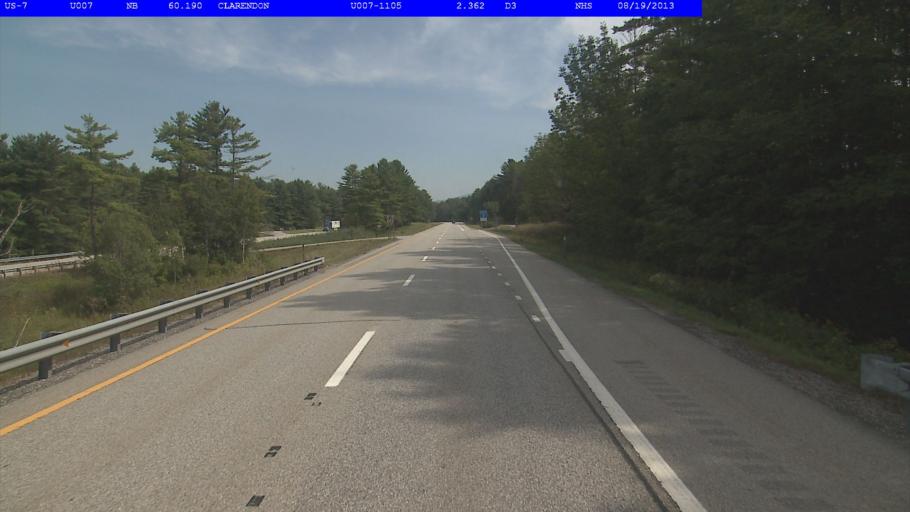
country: US
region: Vermont
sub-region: Rutland County
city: Rutland
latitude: 43.5276
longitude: -72.9627
